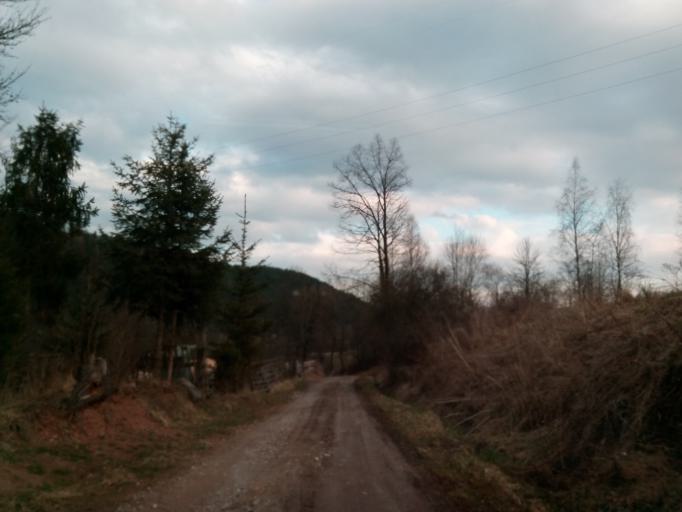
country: SK
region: Kosicky
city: Krompachy
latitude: 48.9506
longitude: 20.9022
